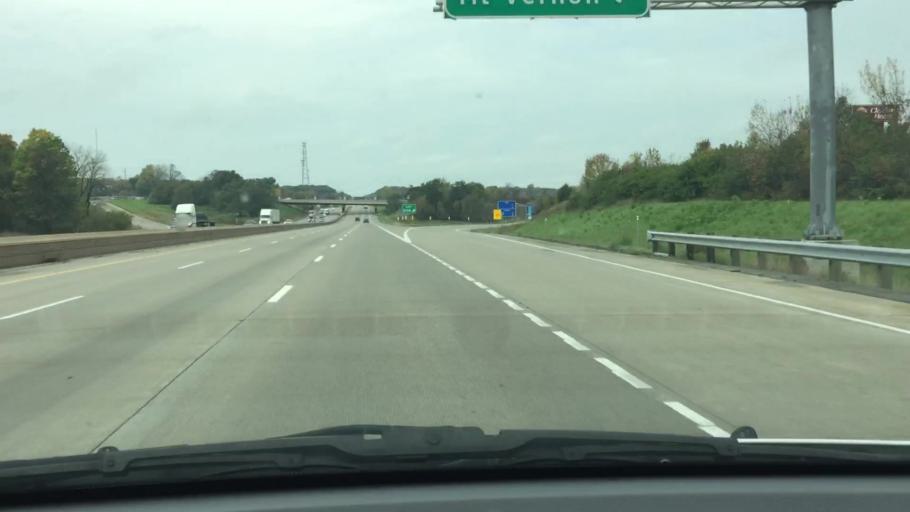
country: US
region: Iowa
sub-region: Johnson County
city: Iowa City
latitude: 41.6862
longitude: -91.4929
